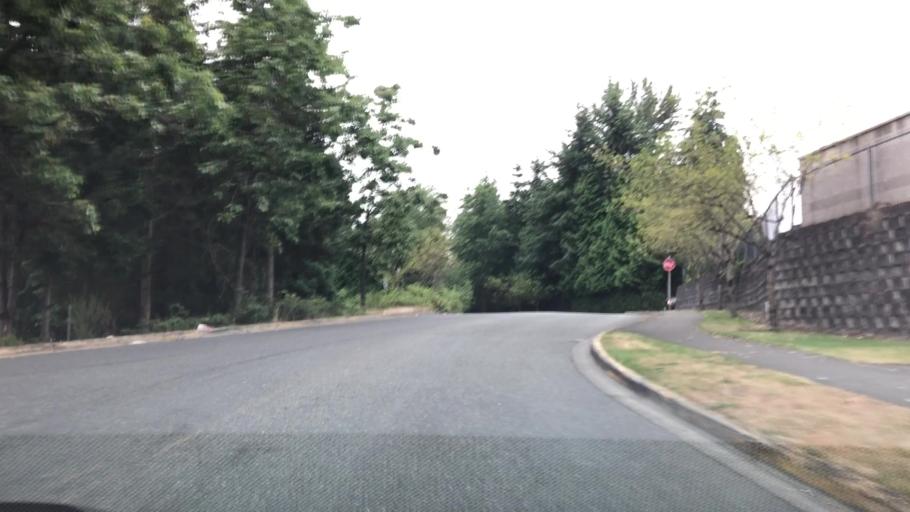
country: US
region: Washington
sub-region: Snohomish County
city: Alderwood Manor
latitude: 47.8205
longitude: -122.2743
